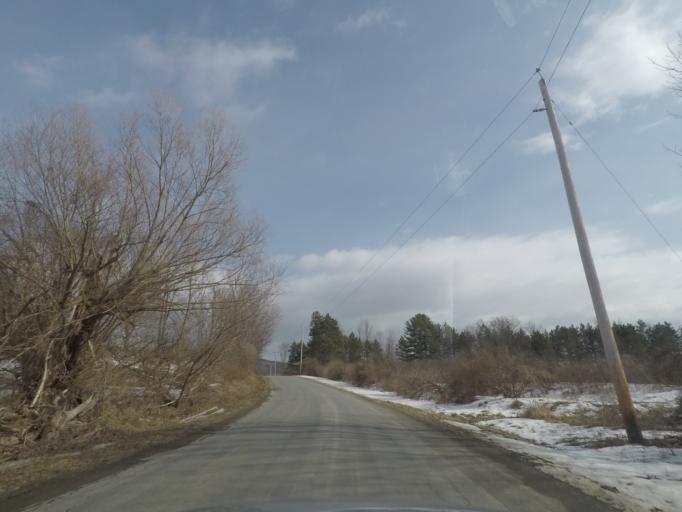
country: US
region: New York
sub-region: Rensselaer County
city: Poestenkill
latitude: 42.7849
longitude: -73.5633
